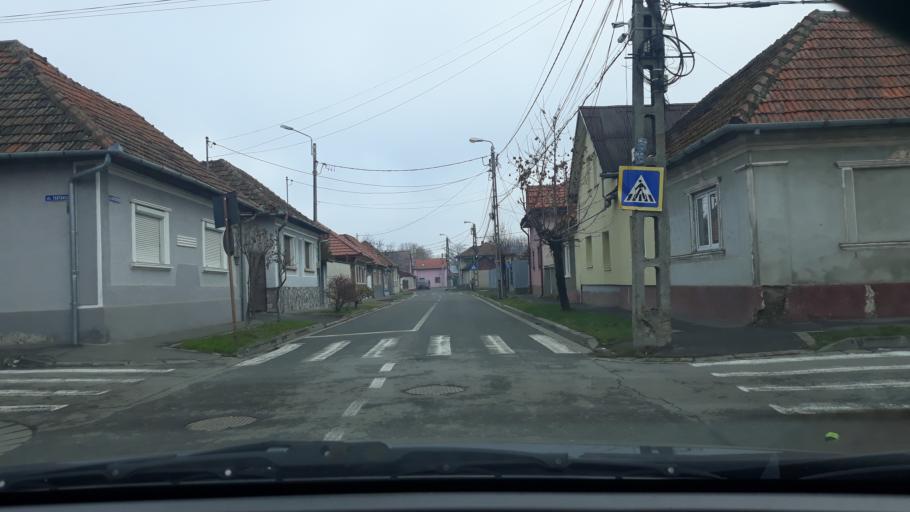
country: RO
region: Bihor
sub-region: Comuna Sanmartin
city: Sanmartin
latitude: 47.0496
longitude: 21.9755
